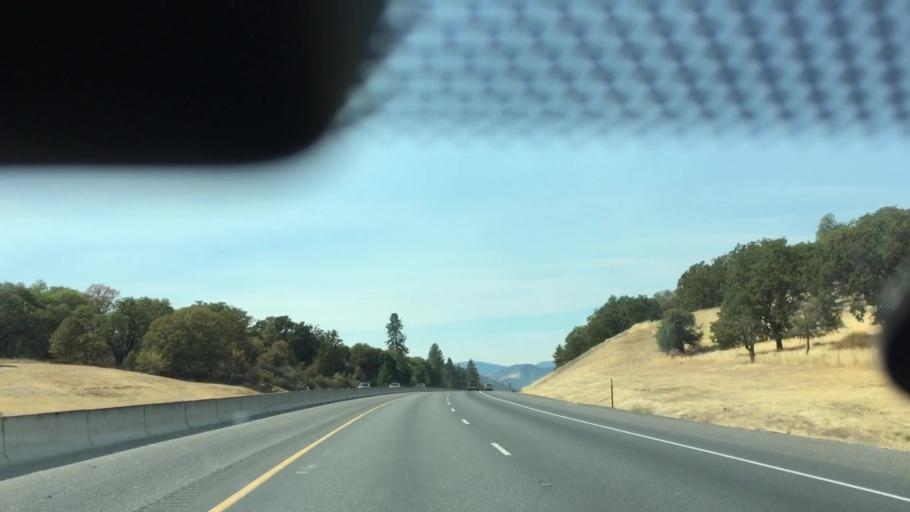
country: US
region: Oregon
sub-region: Jackson County
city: Gold Hill
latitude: 42.4125
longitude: -122.9882
